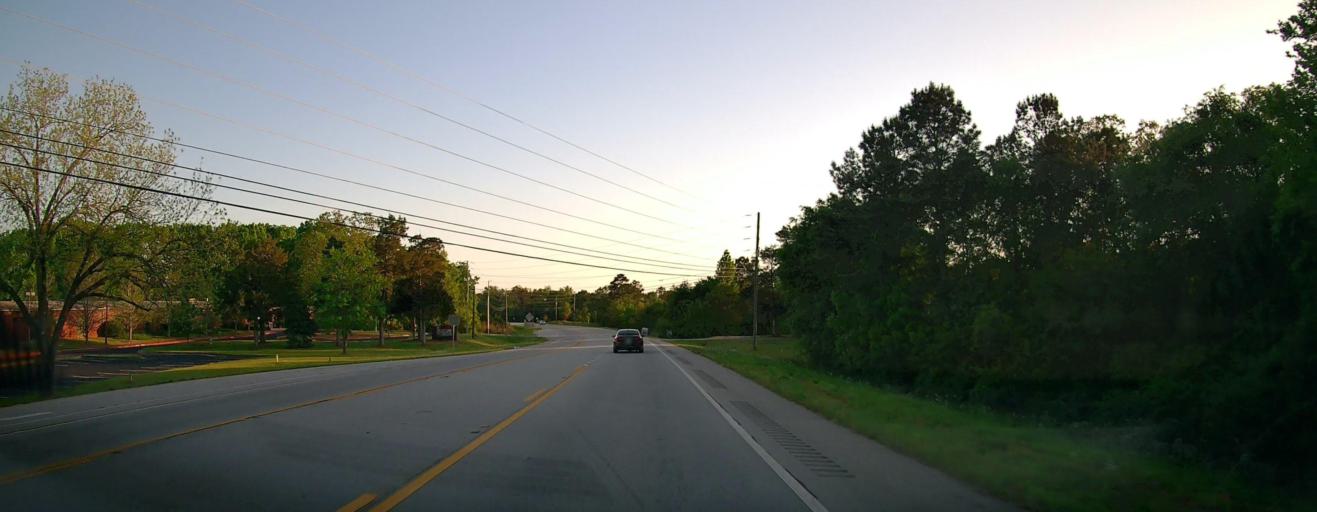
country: US
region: Georgia
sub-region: Newton County
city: Oakwood
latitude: 33.5401
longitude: -83.9506
